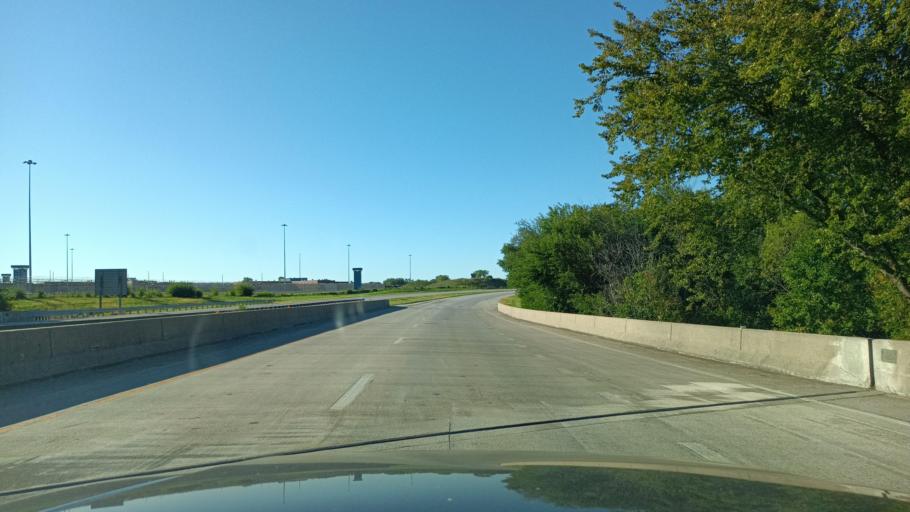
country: US
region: Illinois
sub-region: Knox County
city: Galesburg
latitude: 40.9425
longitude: -90.4101
